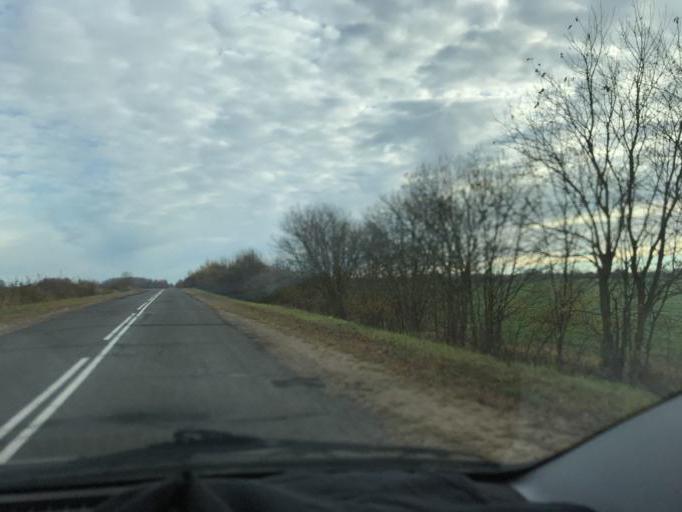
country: BY
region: Vitebsk
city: Haradok
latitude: 55.4103
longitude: 29.7534
